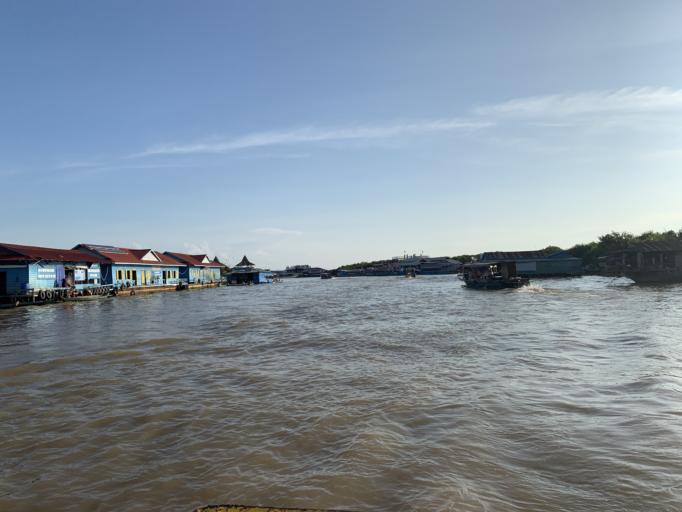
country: KH
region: Siem Reap
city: Siem Reap
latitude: 13.2450
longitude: 103.8230
